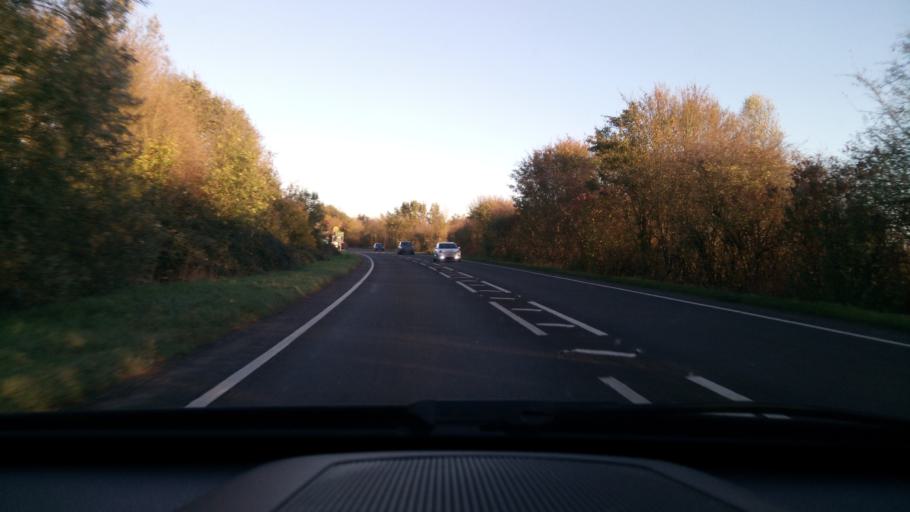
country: GB
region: England
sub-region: Peterborough
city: Glinton
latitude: 52.6326
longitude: -0.3014
